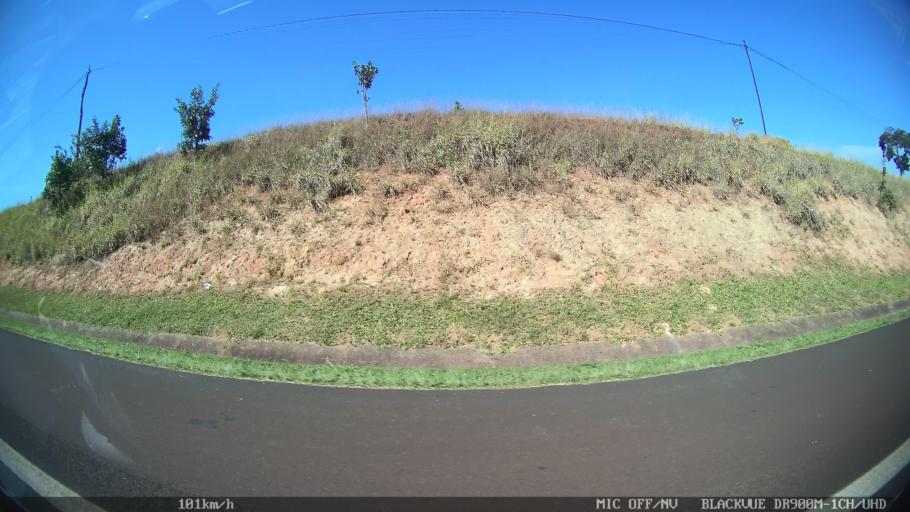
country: BR
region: Sao Paulo
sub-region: Franca
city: Franca
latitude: -20.5657
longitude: -47.4210
